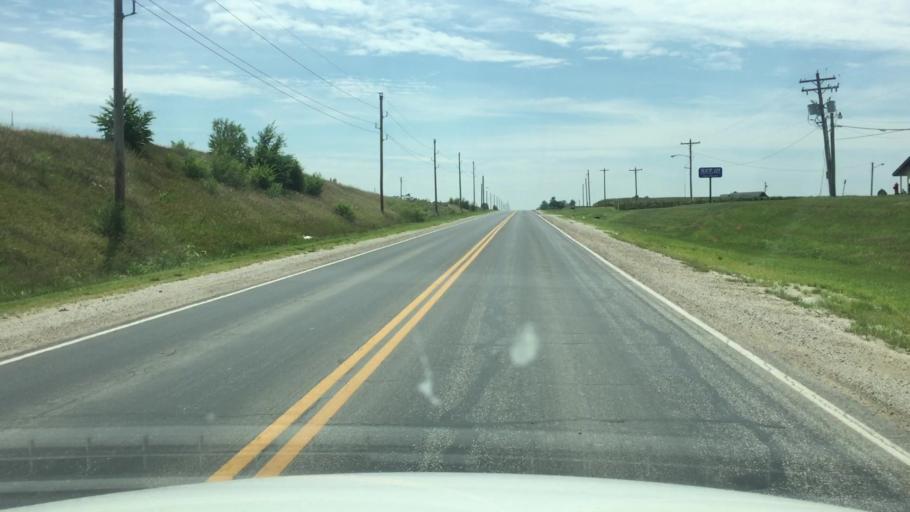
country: US
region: Kansas
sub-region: Nemaha County
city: Sabetha
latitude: 39.8880
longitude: -95.7883
